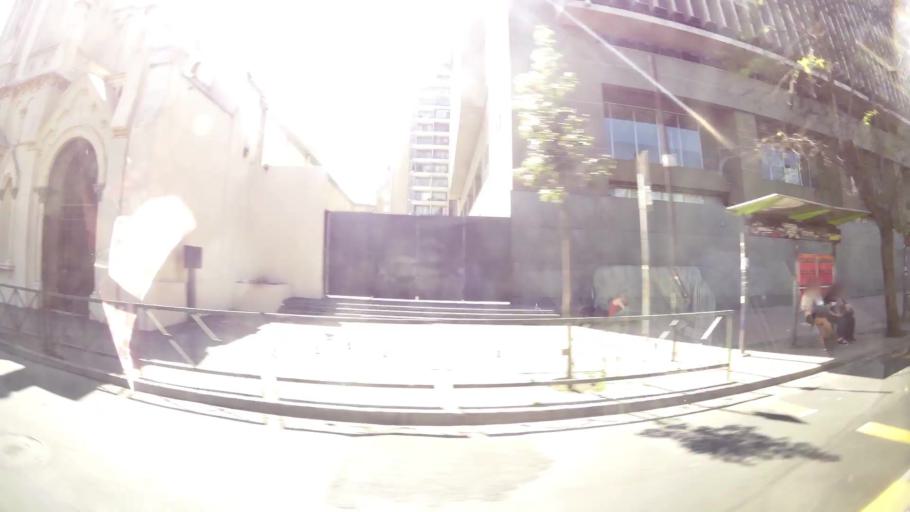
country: CL
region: Santiago Metropolitan
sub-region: Provincia de Santiago
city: Santiago
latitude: -33.4348
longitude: -70.6364
